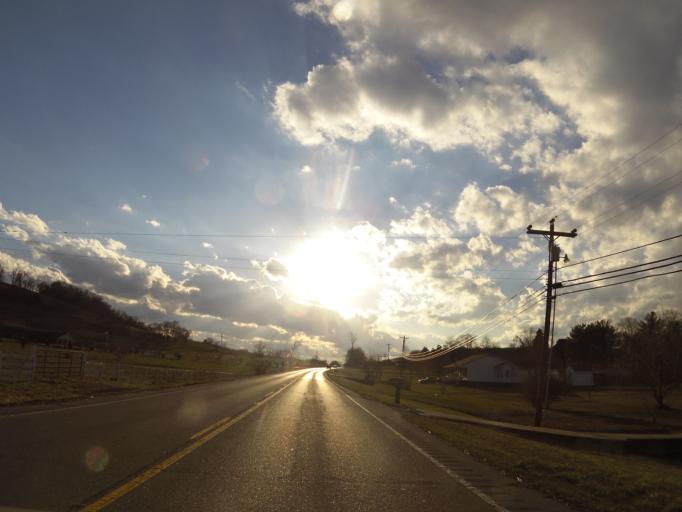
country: US
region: Tennessee
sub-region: Wilson County
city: Lebanon
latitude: 36.2292
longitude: -86.2092
